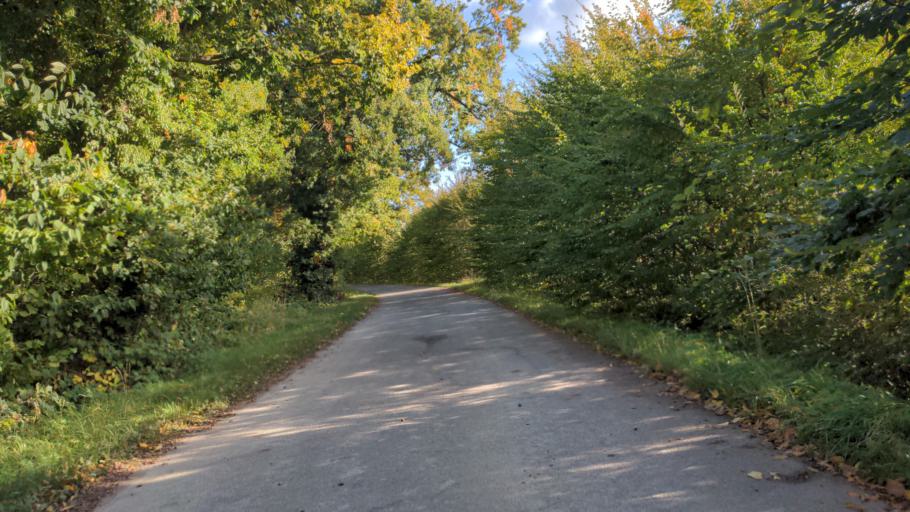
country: DE
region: Schleswig-Holstein
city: Manhagen
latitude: 54.1836
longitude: 10.9137
